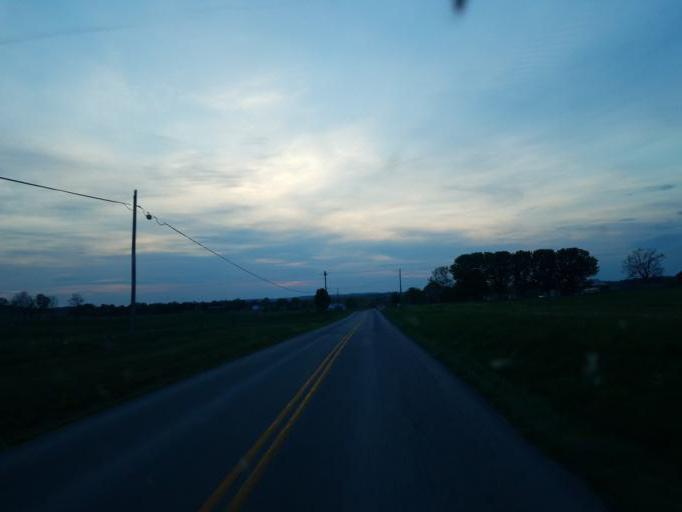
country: US
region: Kentucky
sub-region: Hart County
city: Munfordville
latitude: 37.2643
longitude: -85.8042
